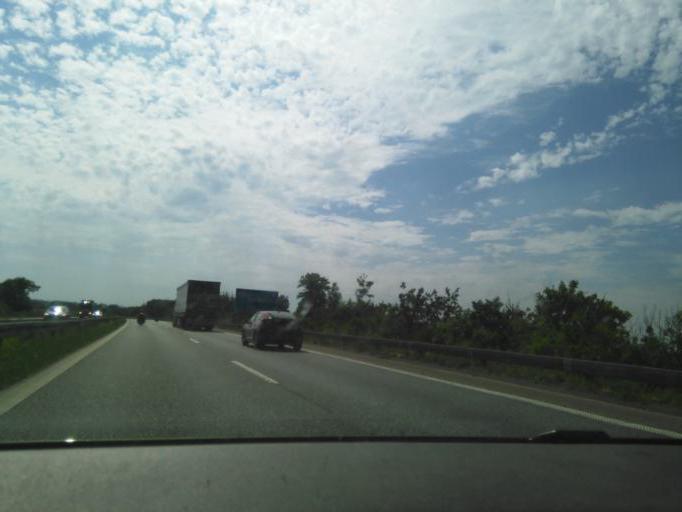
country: DK
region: Zealand
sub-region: Slagelse Kommune
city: Slagelse
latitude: 55.4255
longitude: 11.4244
